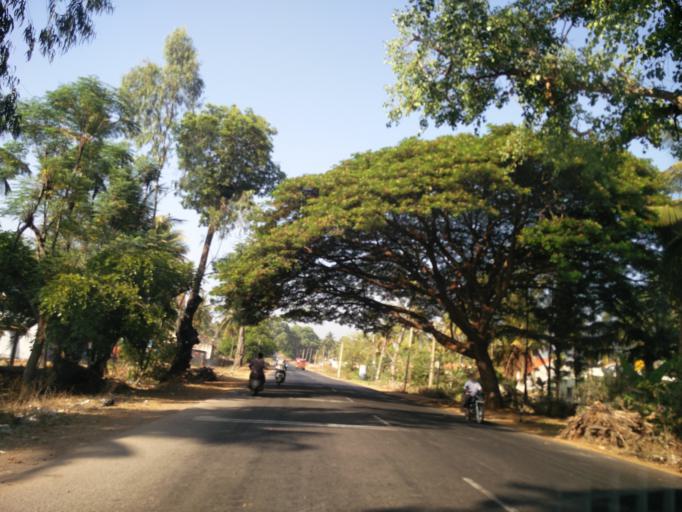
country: IN
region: Karnataka
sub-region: Tumkur
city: Gubbi
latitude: 13.3216
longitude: 76.9637
